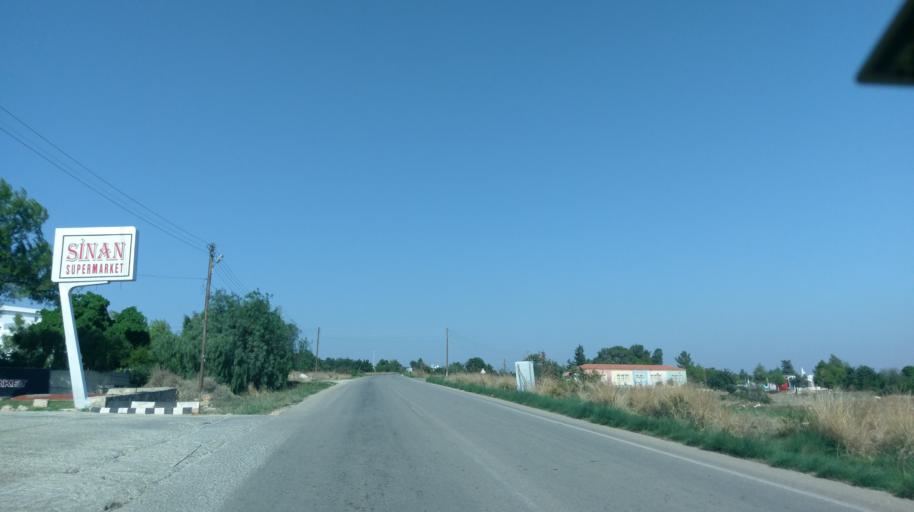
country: CY
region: Ammochostos
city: Leonarisso
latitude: 35.4227
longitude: 34.1259
